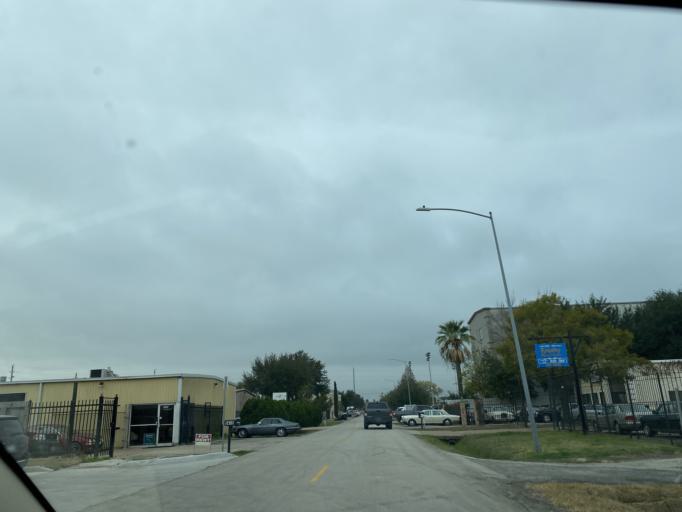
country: US
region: Texas
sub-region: Harris County
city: Bellaire
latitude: 29.7289
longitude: -95.4771
